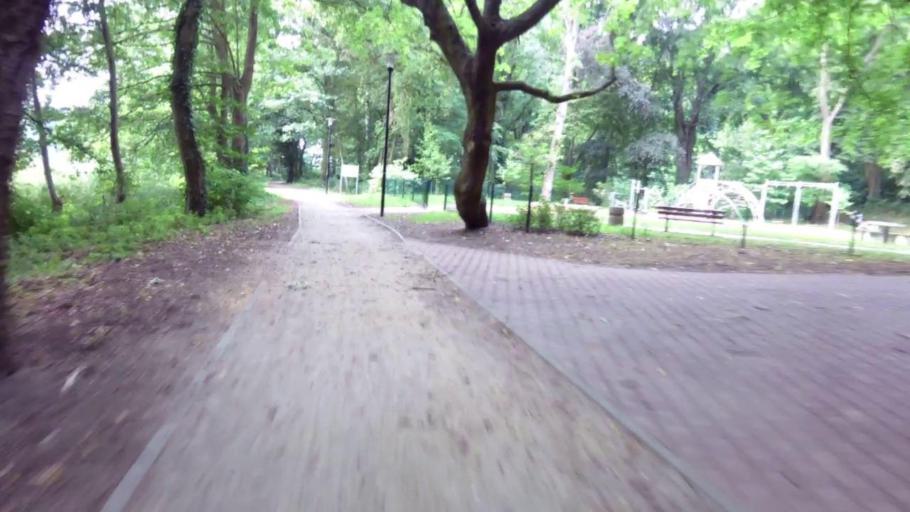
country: PL
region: West Pomeranian Voivodeship
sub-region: Powiat choszczenski
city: Choszczno
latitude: 53.1578
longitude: 15.4303
